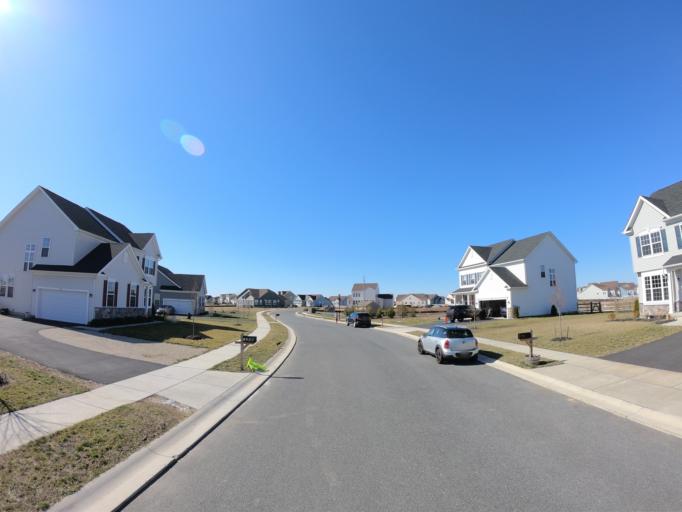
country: US
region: Delaware
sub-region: New Castle County
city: Middletown
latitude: 39.5161
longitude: -75.6585
